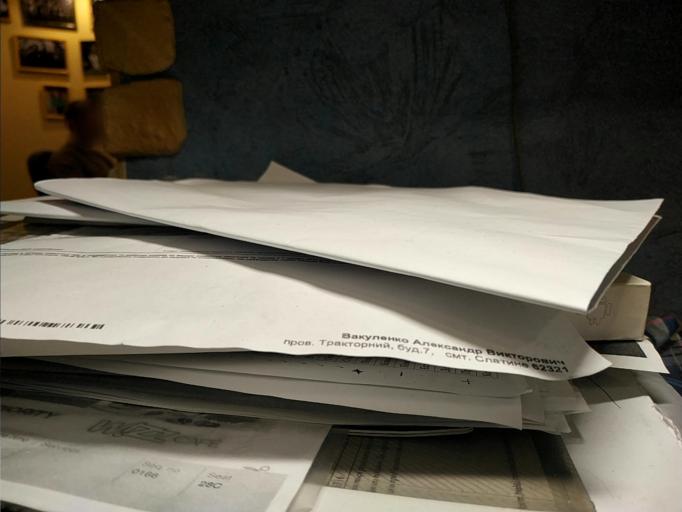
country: RU
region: Tverskaya
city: Zubtsov
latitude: 56.1071
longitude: 34.6483
